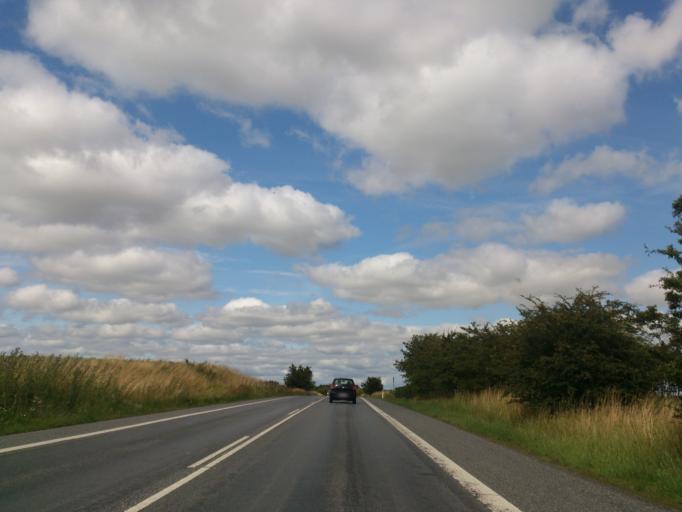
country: DK
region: South Denmark
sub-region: Aabenraa Kommune
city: Krusa
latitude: 54.8920
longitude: 9.4263
